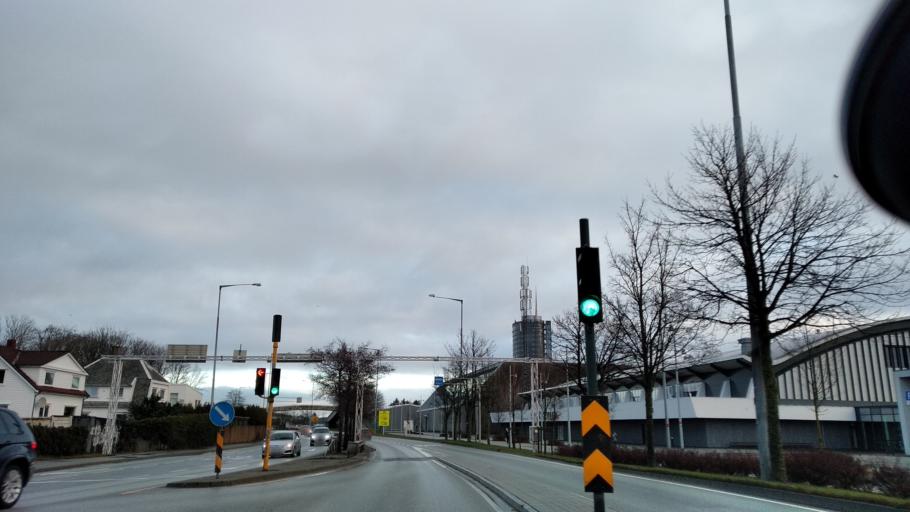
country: NO
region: Rogaland
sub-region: Stavanger
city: Stavanger
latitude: 58.9543
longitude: 5.6930
